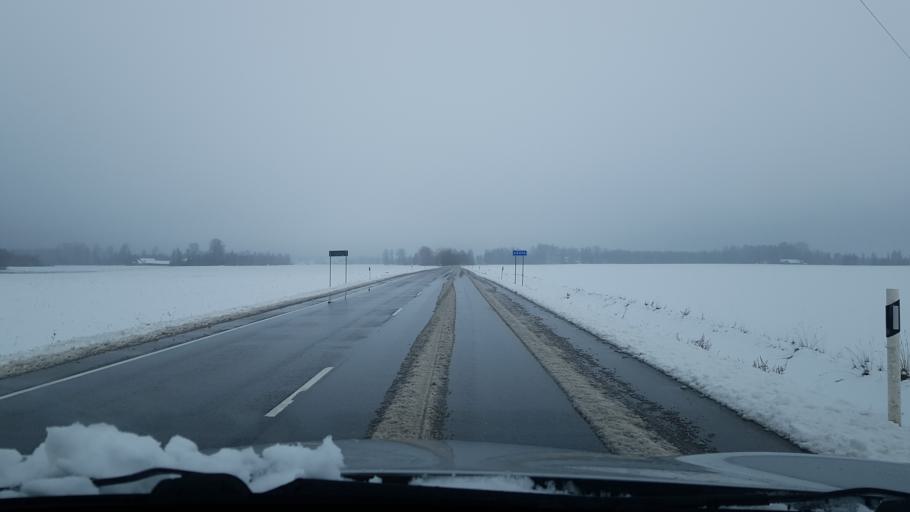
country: EE
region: Vorumaa
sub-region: Voru linn
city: Voru
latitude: 57.8591
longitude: 27.0914
